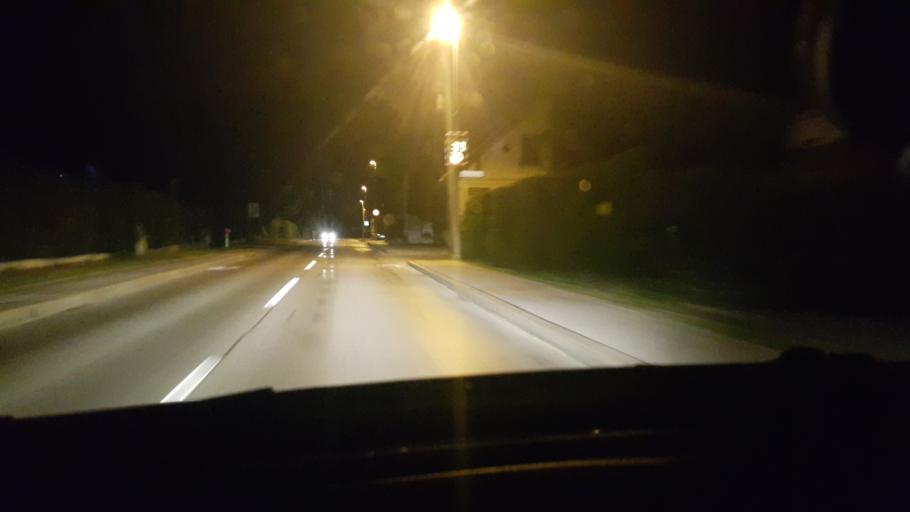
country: SI
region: Domzale
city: Domzale
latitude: 46.1362
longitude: 14.5827
